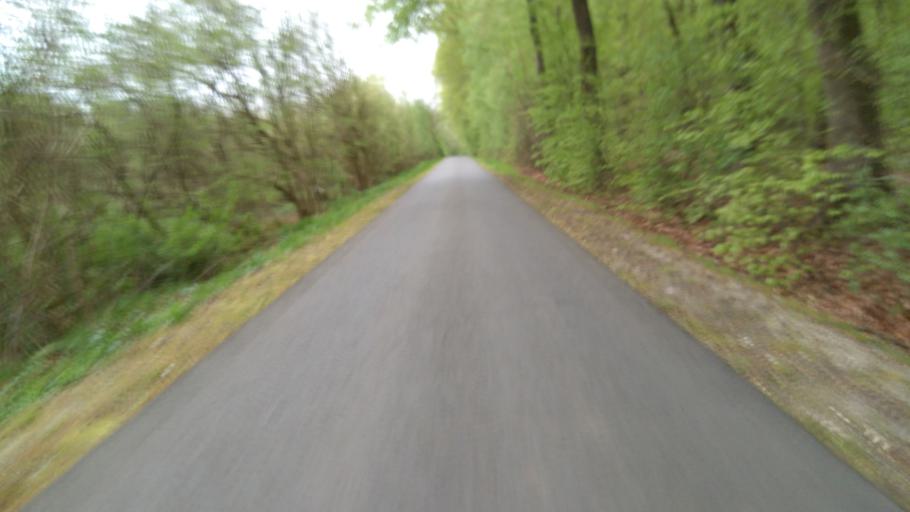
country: DE
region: Lower Saxony
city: Bliedersdorf
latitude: 53.4563
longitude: 9.5528
